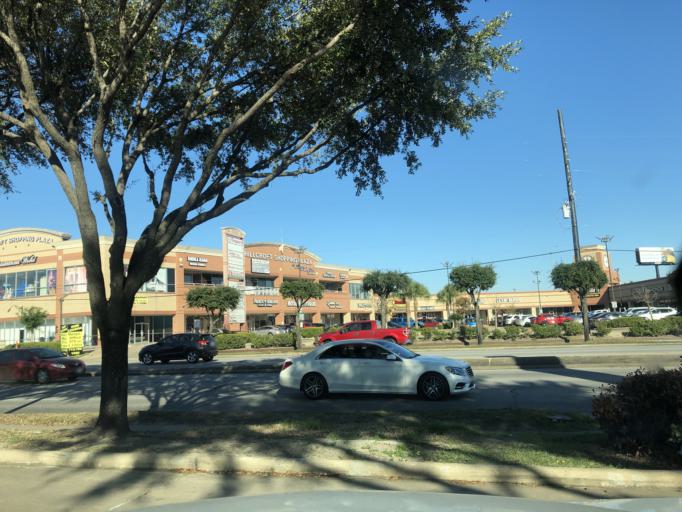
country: US
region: Texas
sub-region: Harris County
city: Bellaire
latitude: 29.7182
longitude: -95.5008
